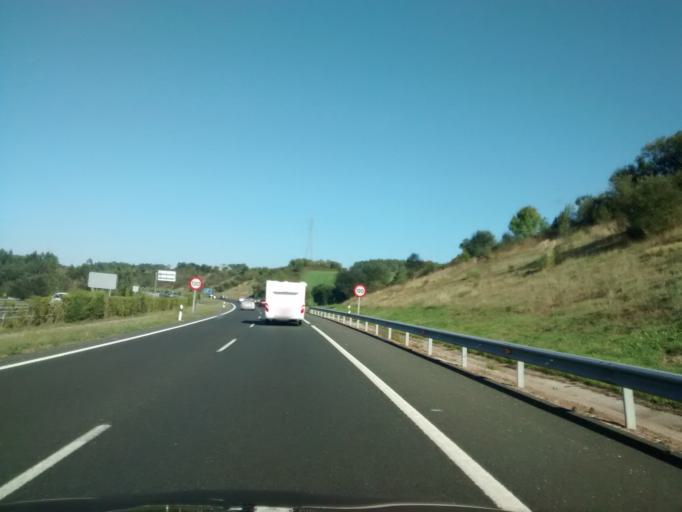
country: ES
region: Cantabria
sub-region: Provincia de Cantabria
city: Cabezon de la Sal
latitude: 43.3163
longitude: -4.2419
